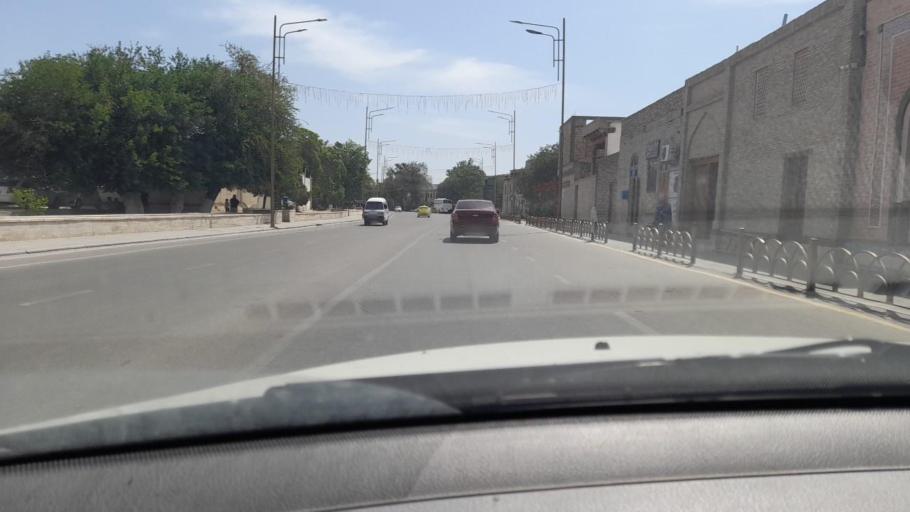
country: UZ
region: Bukhara
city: Bukhara
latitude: 39.7732
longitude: 64.4250
